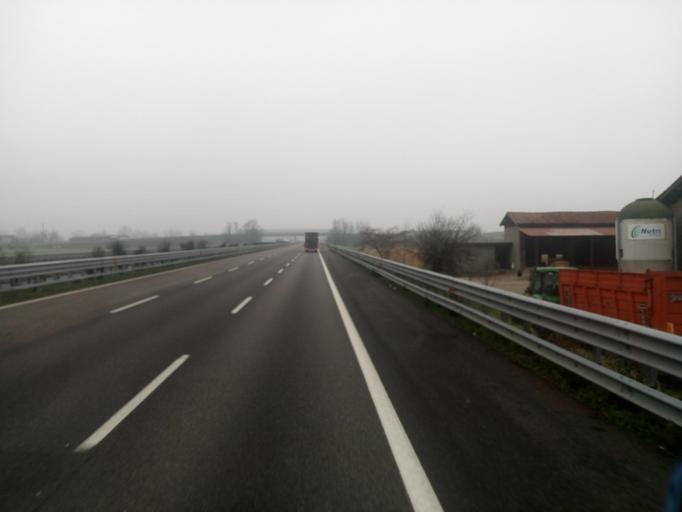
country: IT
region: Lombardy
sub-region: Provincia di Brescia
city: Bagnolo Mella
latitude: 45.4254
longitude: 10.2000
